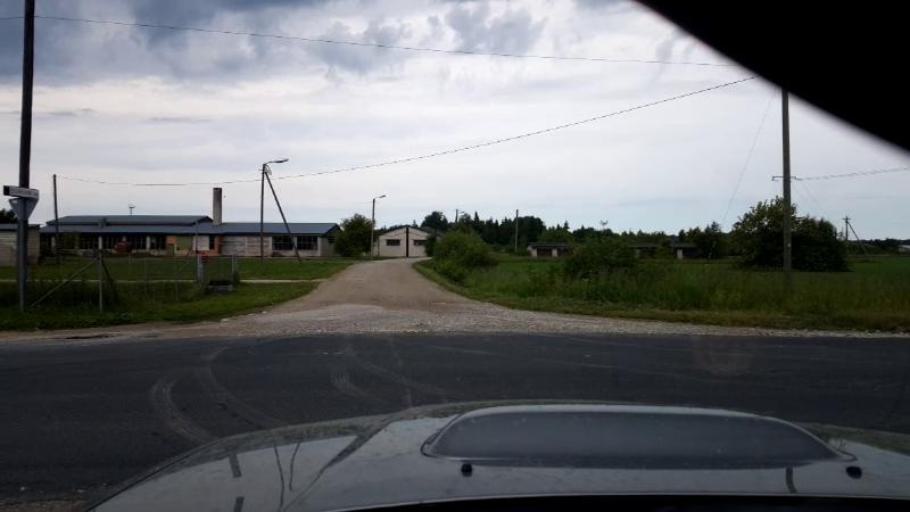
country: EE
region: Paernumaa
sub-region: Tootsi vald
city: Tootsi
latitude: 58.5293
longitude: 24.7039
